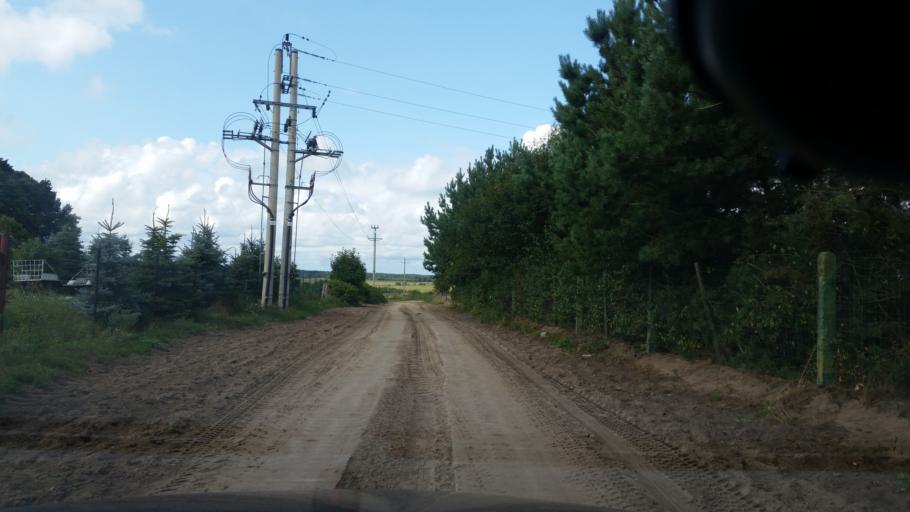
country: PL
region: Pomeranian Voivodeship
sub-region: Powiat wejherowski
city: Choczewo
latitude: 54.7709
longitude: 17.7960
